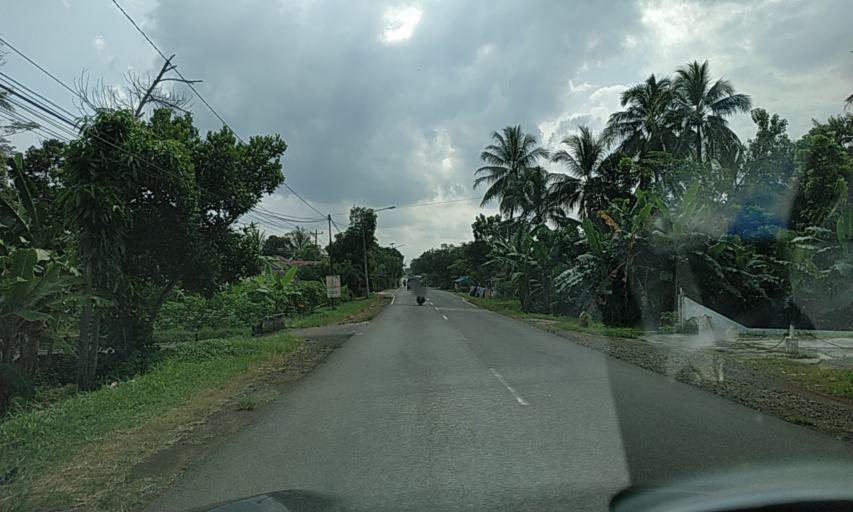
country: ID
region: Central Java
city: Winangun
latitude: -7.3414
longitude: 108.7070
